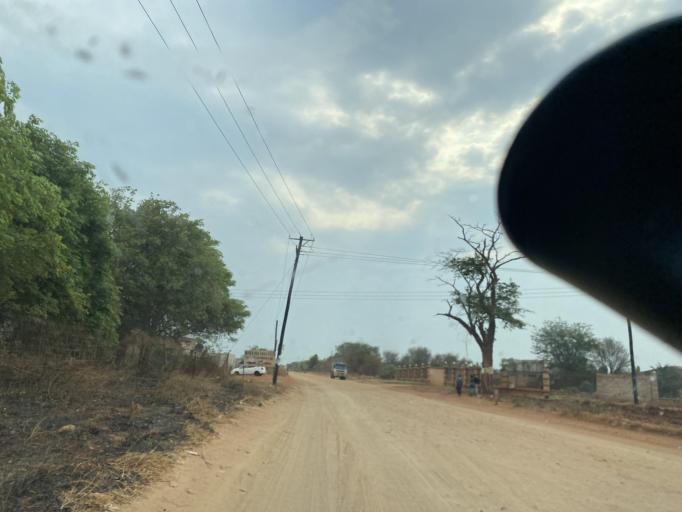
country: ZM
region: Lusaka
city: Lusaka
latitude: -15.2907
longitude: 28.2760
